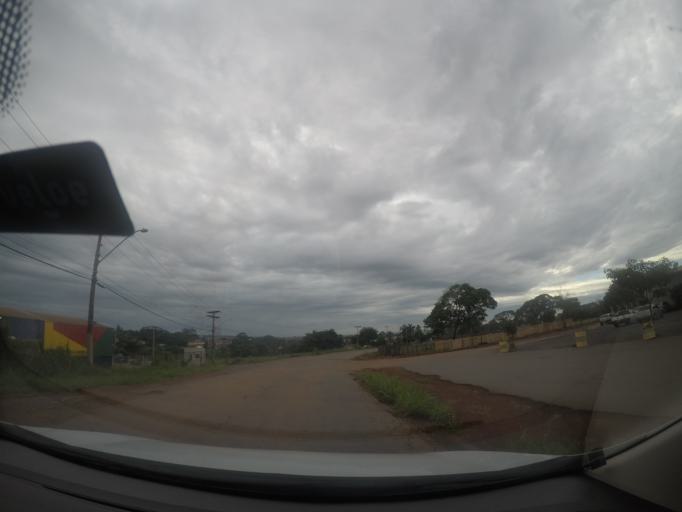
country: BR
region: Goias
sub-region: Goiania
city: Goiania
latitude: -16.6381
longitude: -49.3411
